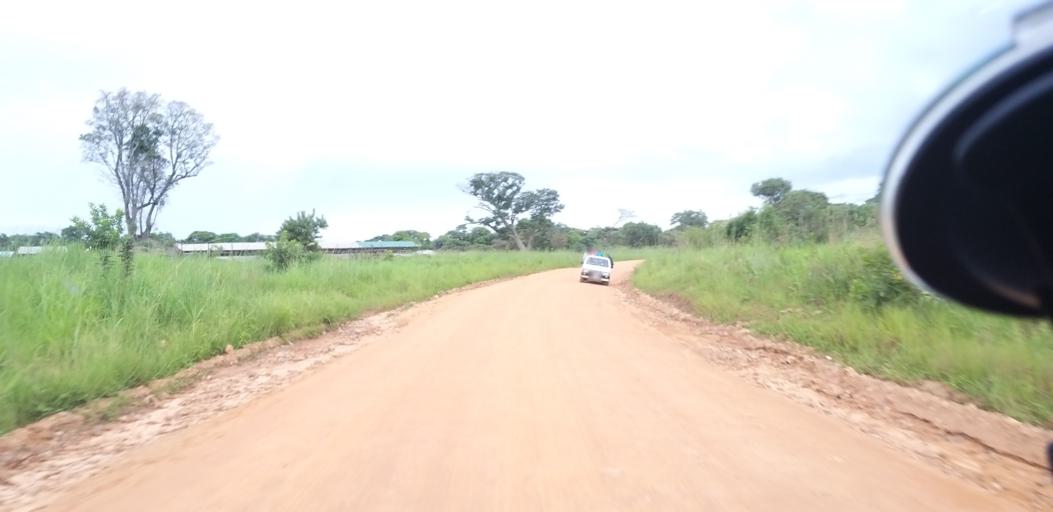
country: ZM
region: Lusaka
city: Lusaka
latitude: -15.1959
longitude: 28.4433
